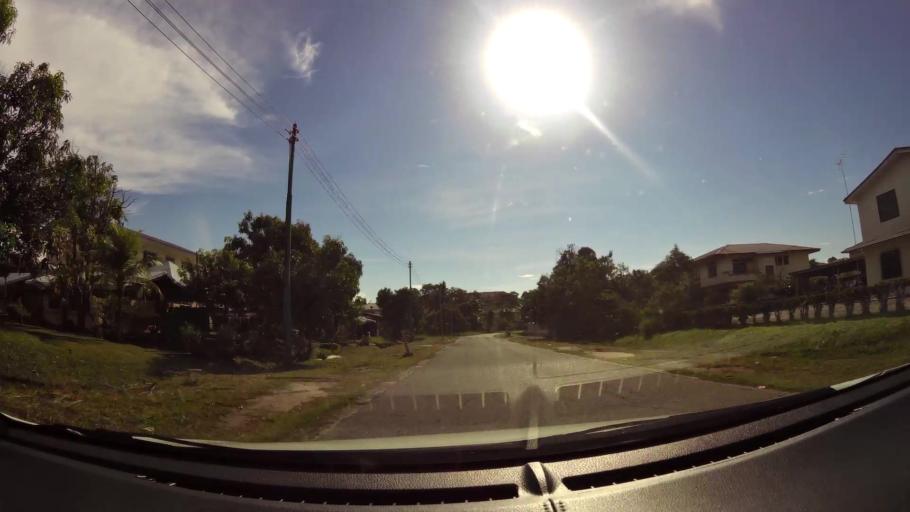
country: BN
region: Brunei and Muara
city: Bandar Seri Begawan
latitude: 4.9641
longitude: 114.9544
